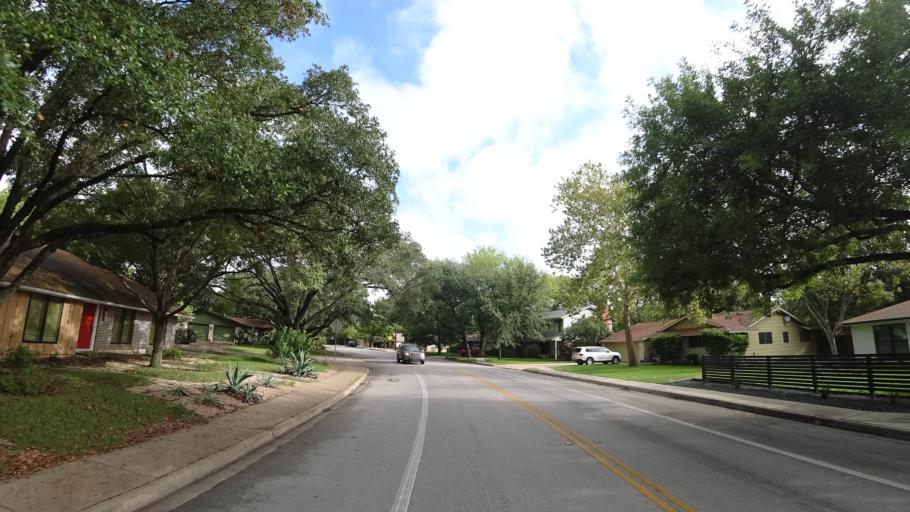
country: US
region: Texas
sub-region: Travis County
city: West Lake Hills
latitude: 30.3561
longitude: -97.7399
